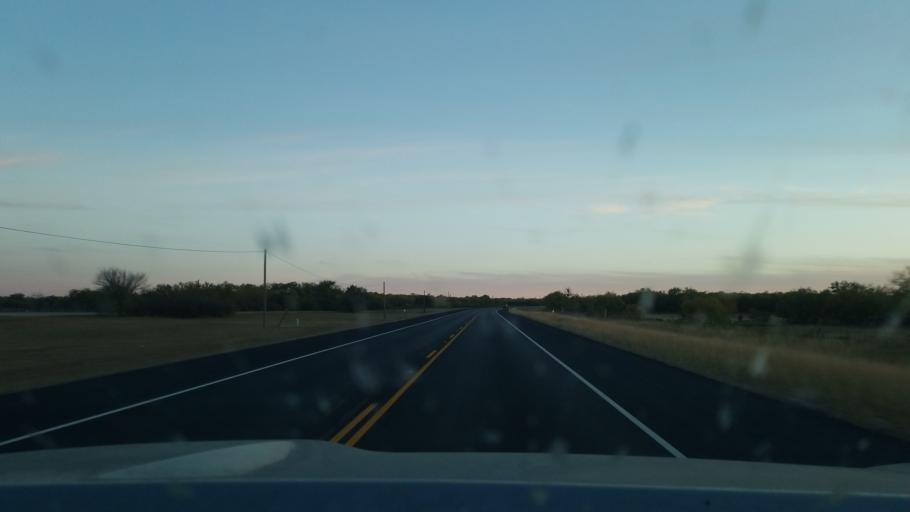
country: US
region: Texas
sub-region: Stephens County
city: Breckenridge
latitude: 32.6148
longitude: -98.9007
